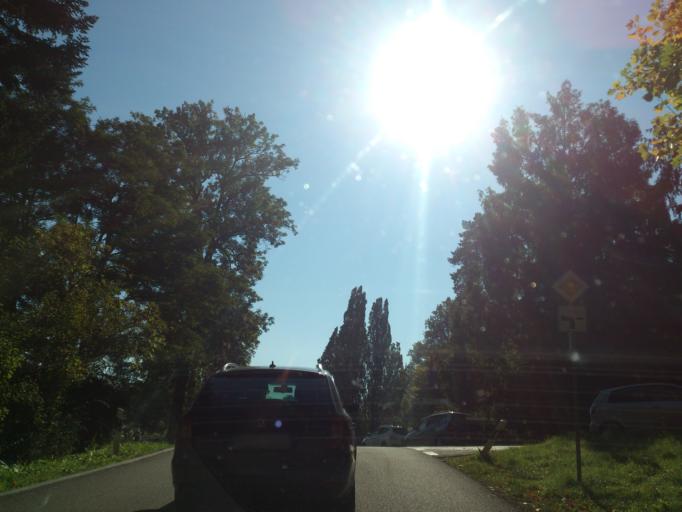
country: DE
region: Hesse
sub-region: Regierungsbezirk Kassel
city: Baunatal
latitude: 51.3173
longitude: 9.4132
